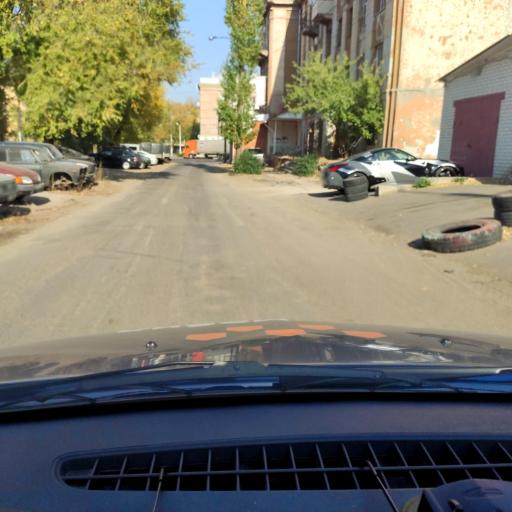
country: RU
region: Voronezj
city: Voronezh
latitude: 51.6340
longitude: 39.2412
